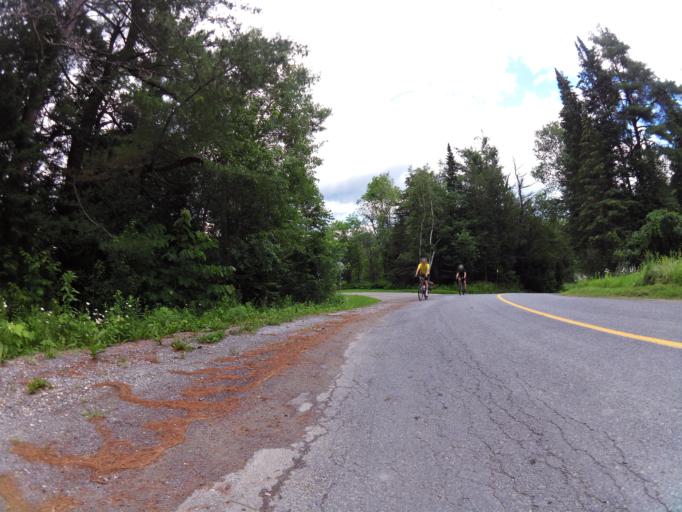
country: CA
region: Ontario
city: Renfrew
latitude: 45.0437
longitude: -76.7010
